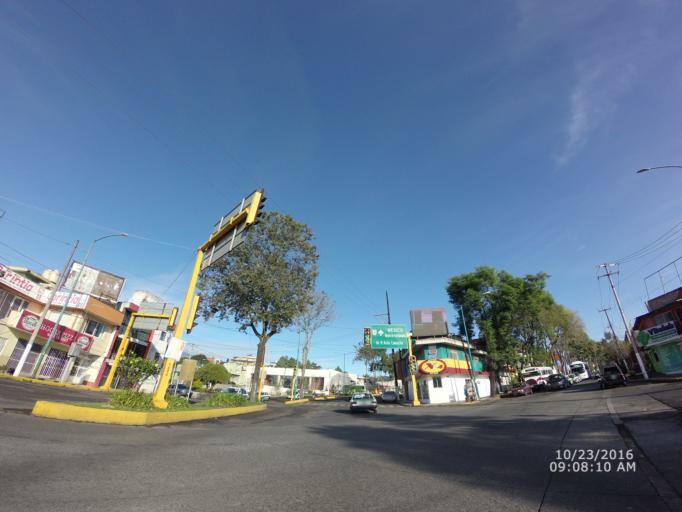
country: TR
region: Canakkale
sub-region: Goekceada
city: Gokceada
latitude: 40.2203
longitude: 26.0310
